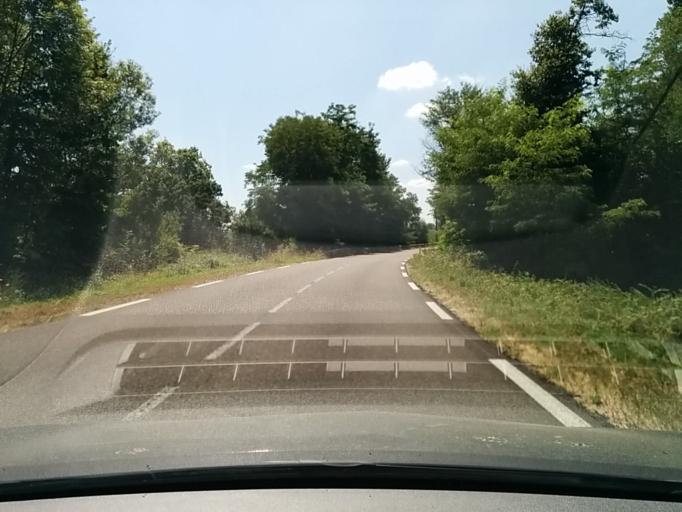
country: FR
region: Midi-Pyrenees
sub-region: Departement du Gers
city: Nogaro
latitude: 43.7912
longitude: 0.0182
